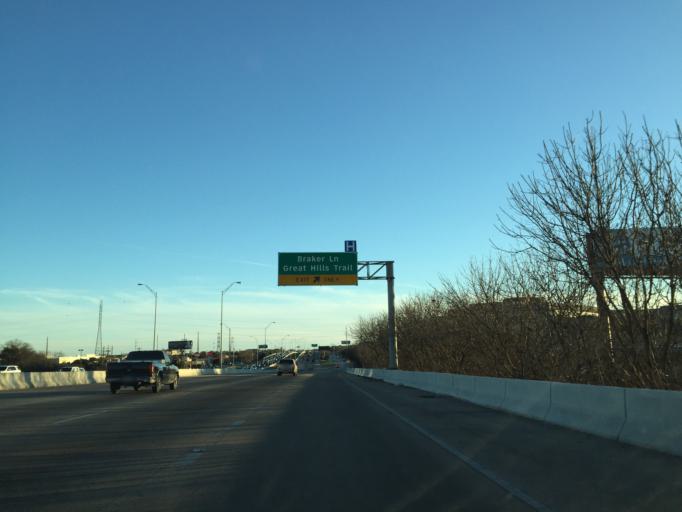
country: US
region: Texas
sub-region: Williamson County
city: Jollyville
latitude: 30.4070
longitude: -97.7455
